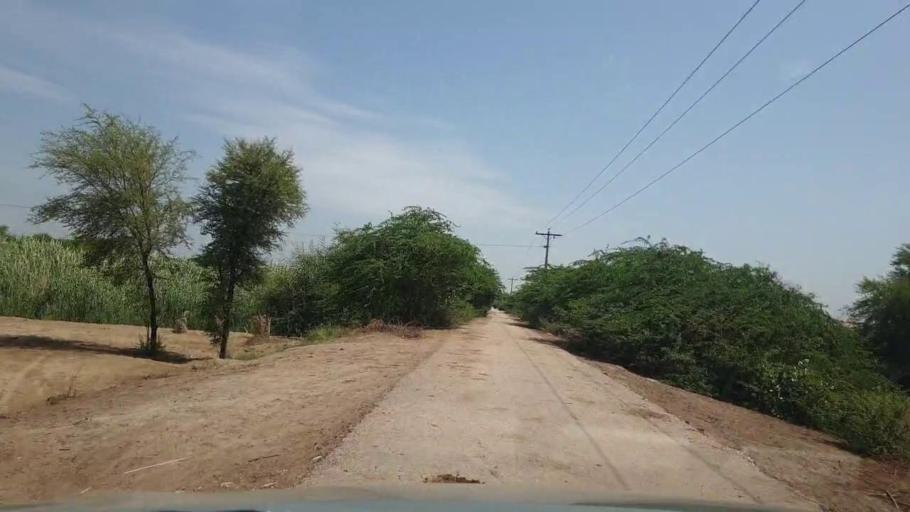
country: PK
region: Sindh
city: Bozdar
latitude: 27.1089
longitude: 68.9832
